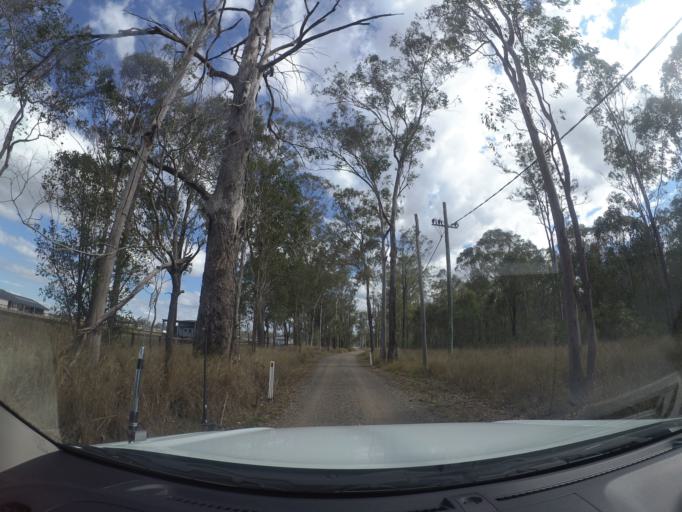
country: AU
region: Queensland
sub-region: Logan
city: North Maclean
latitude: -27.8081
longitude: 152.9934
